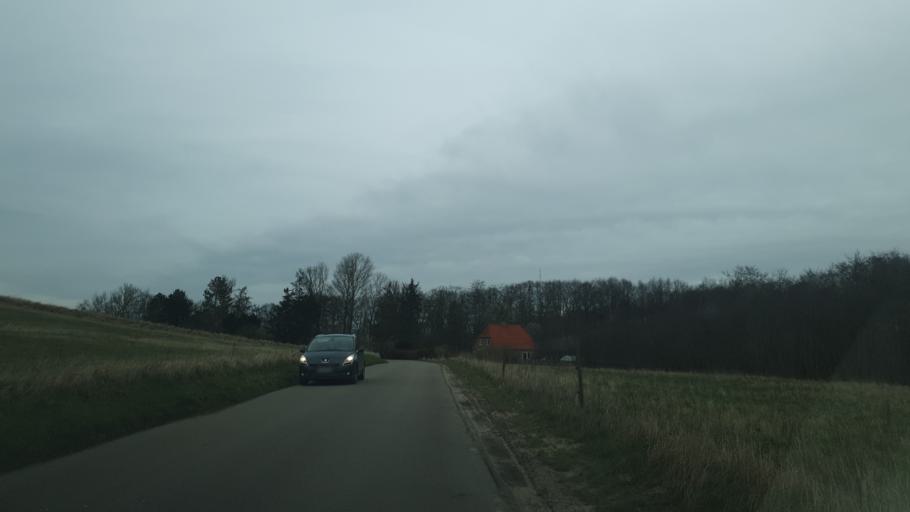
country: DK
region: Zealand
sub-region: Odsherred Kommune
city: Asnaes
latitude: 55.8292
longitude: 11.4272
